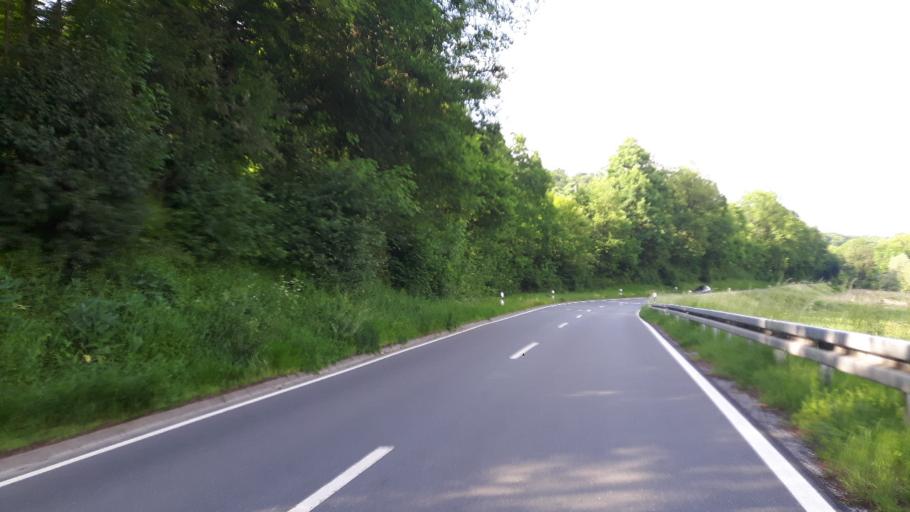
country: DE
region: Bavaria
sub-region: Regierungsbezirk Unterfranken
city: Reichenberg
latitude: 49.7360
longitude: 9.9188
